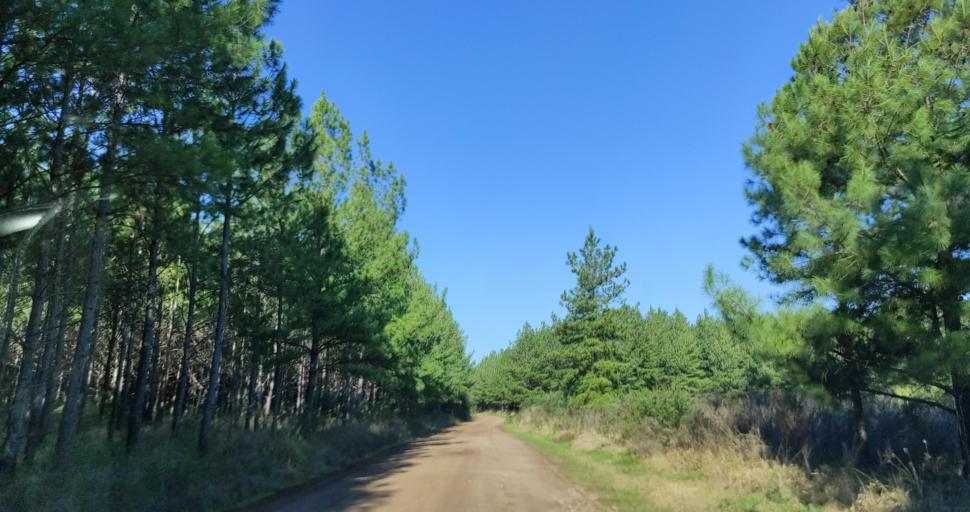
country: AR
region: Misiones
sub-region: Departamento de Apostoles
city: San Jose
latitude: -27.6781
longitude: -55.6571
